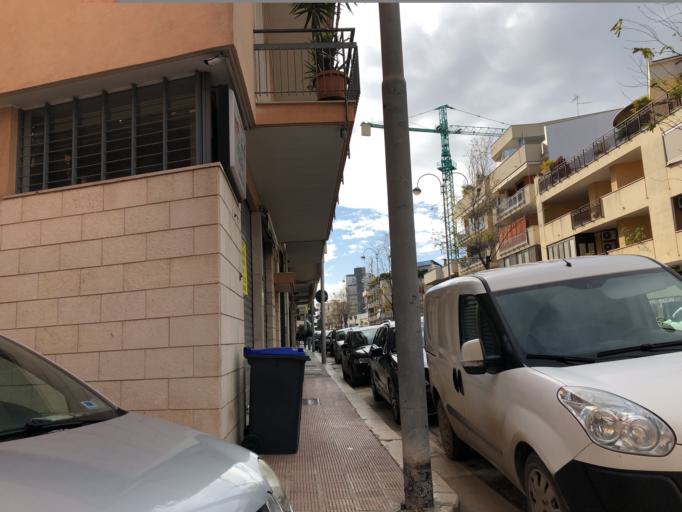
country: IT
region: Apulia
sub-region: Provincia di Barletta - Andria - Trani
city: Andria
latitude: 41.2212
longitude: 16.3064
